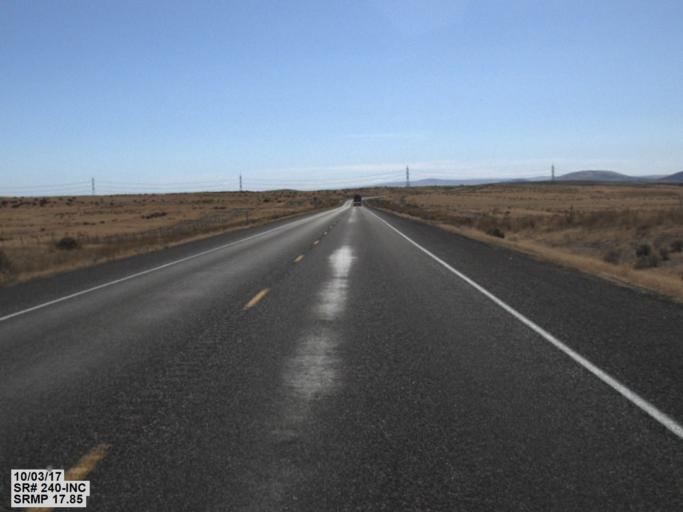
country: US
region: Washington
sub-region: Benton County
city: West Richland
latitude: 46.4130
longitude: -119.4560
